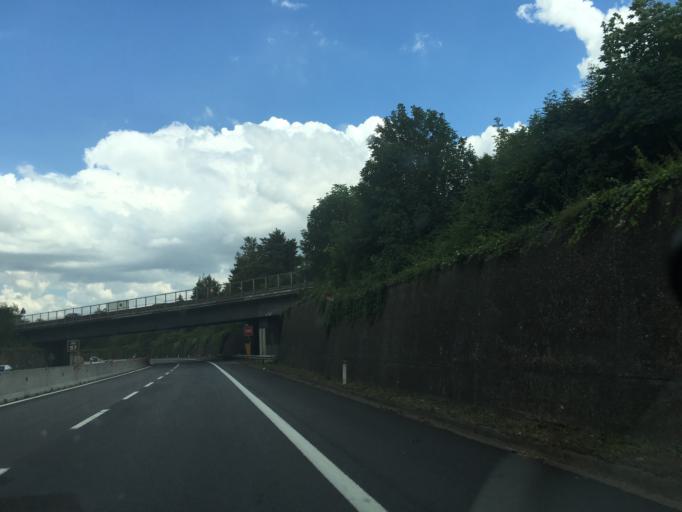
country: IT
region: Campania
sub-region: Provincia di Avellino
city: Grottaminarda
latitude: 41.0603
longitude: 15.0444
